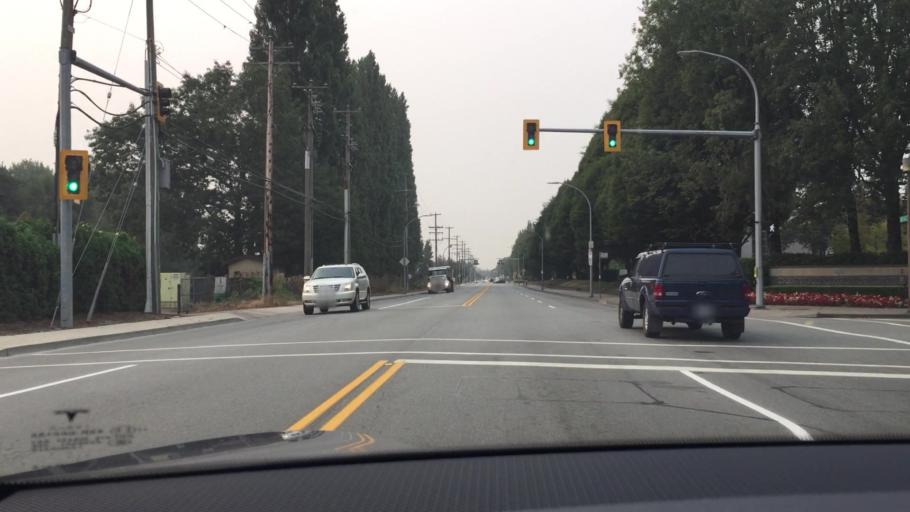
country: CA
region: British Columbia
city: Richmond
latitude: 49.1766
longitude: -123.0692
